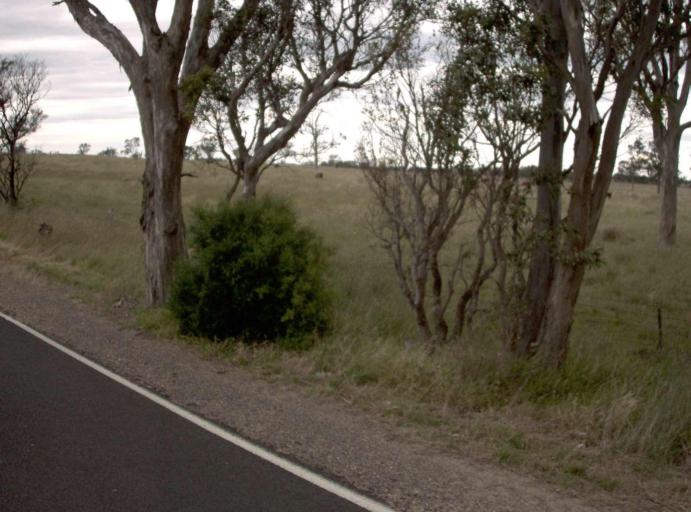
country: AU
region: Victoria
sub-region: Wellington
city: Sale
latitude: -38.0009
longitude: 147.1912
